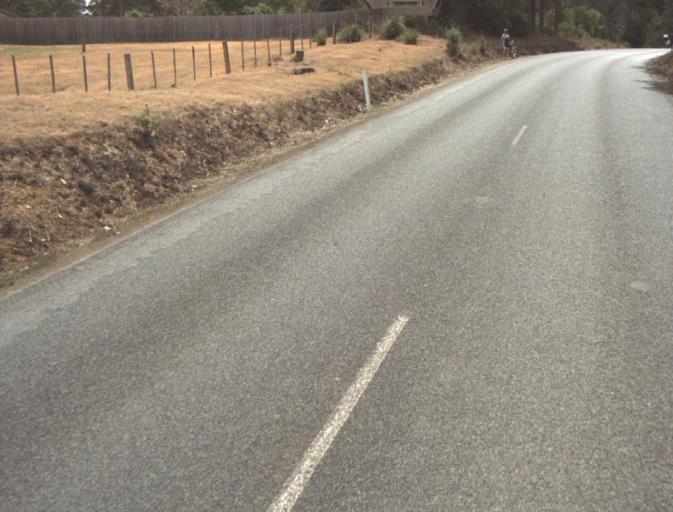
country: AU
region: Tasmania
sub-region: Launceston
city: Mayfield
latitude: -41.2162
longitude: 147.2098
